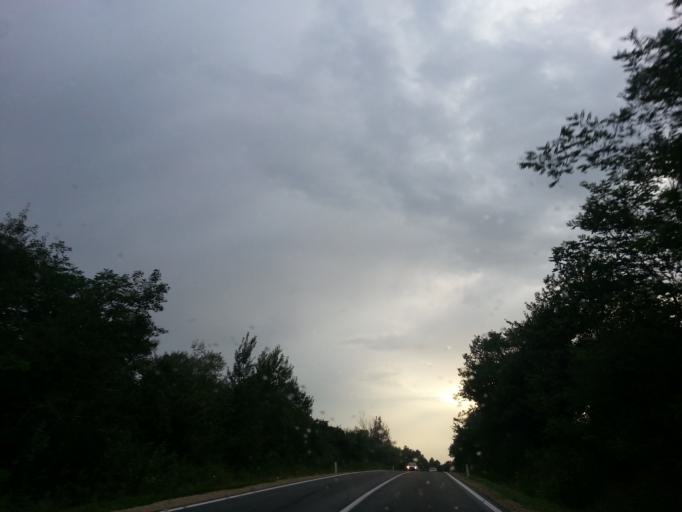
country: HR
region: Vukovarsko-Srijemska
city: Gunja
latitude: 44.8472
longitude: 18.9414
